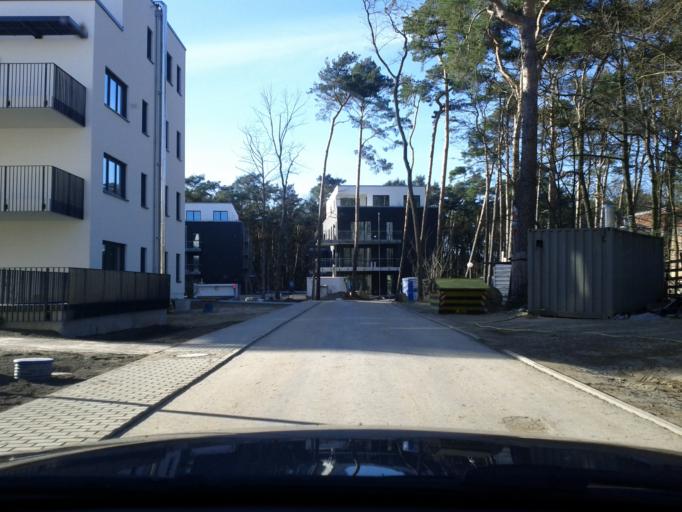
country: DE
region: Berlin
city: Dahlem
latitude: 52.4486
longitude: 13.2675
